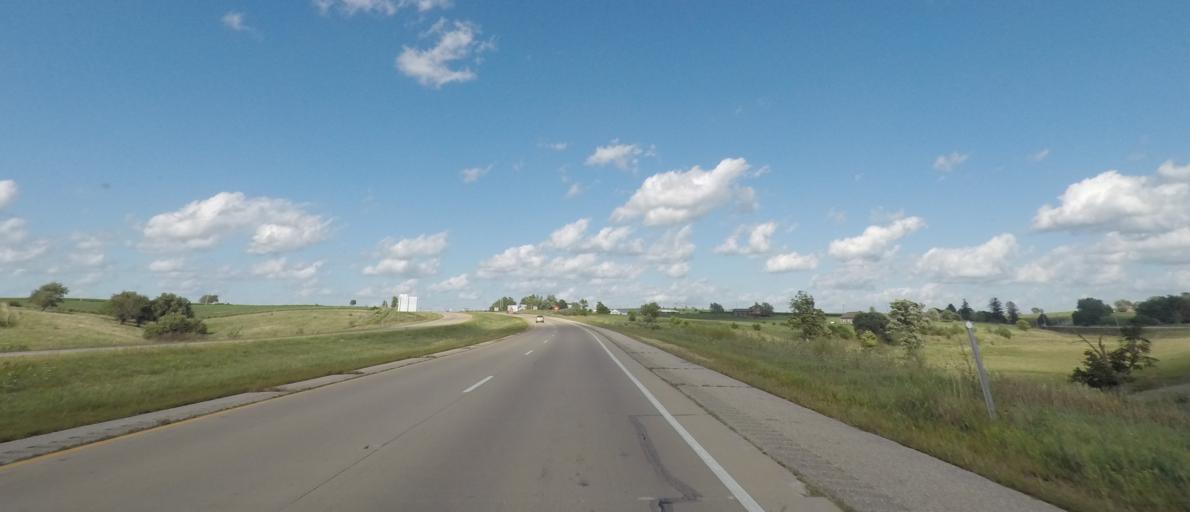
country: US
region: Wisconsin
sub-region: Iowa County
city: Mineral Point
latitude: 42.9016
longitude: -90.1456
